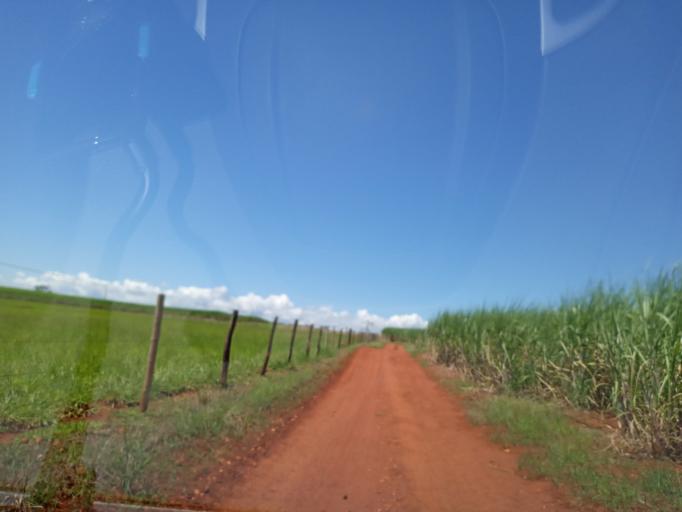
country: BR
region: Goias
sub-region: Itumbiara
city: Itumbiara
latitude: -18.4023
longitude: -49.1300
